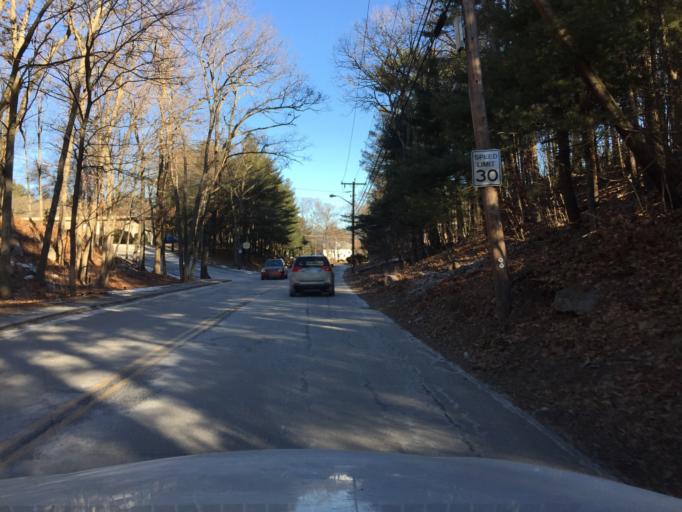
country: US
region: Massachusetts
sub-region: Norfolk County
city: Foxborough
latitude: 42.0587
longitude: -71.2357
